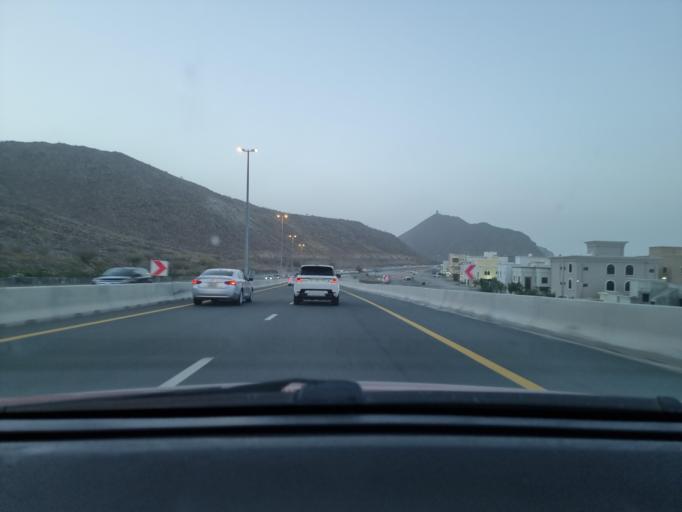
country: AE
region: Ash Shariqah
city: Khawr Fakkan
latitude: 25.3355
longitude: 56.3371
